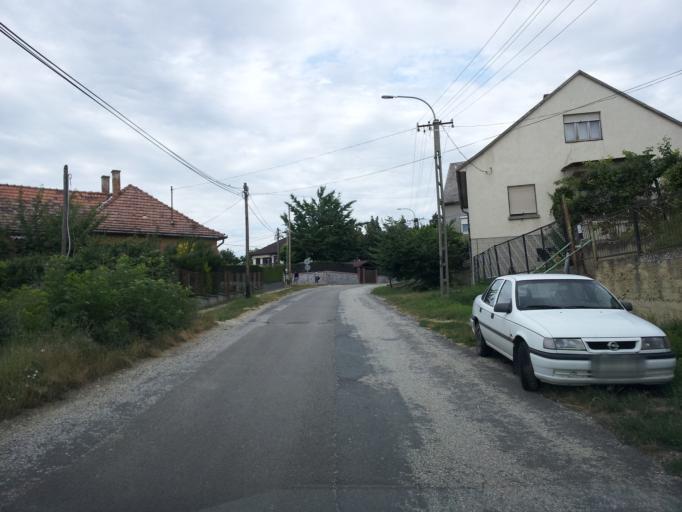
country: HU
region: Fejer
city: Enying
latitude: 46.9281
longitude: 18.2400
